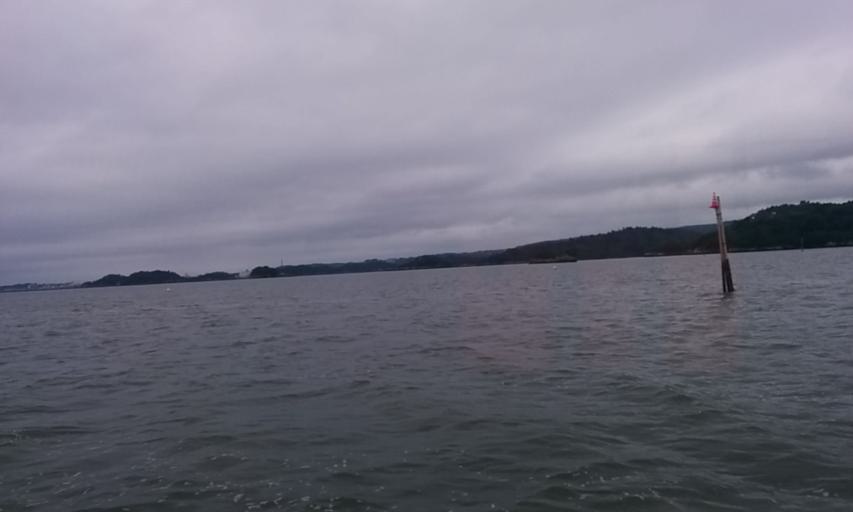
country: JP
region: Miyagi
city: Matsushima
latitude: 38.3513
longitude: 141.0743
